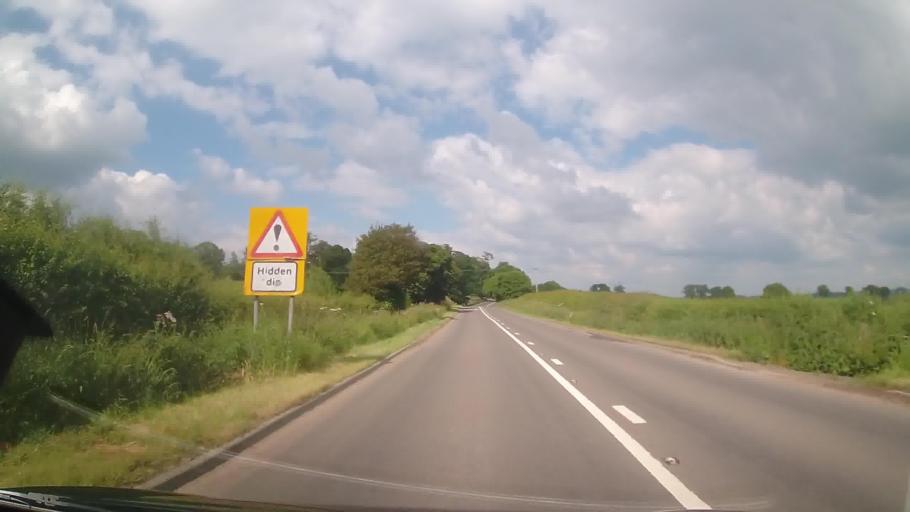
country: GB
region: England
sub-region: Shropshire
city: Ellesmere
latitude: 52.8966
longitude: -2.9312
